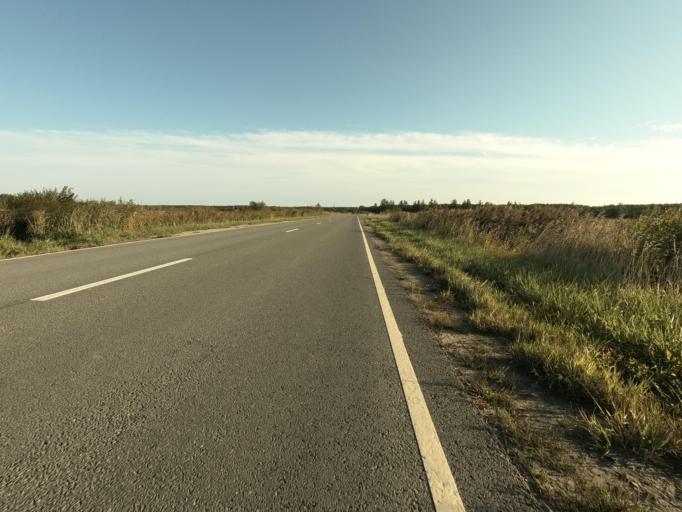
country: RU
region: St.-Petersburg
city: Sapernyy
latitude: 59.7331
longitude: 30.6577
